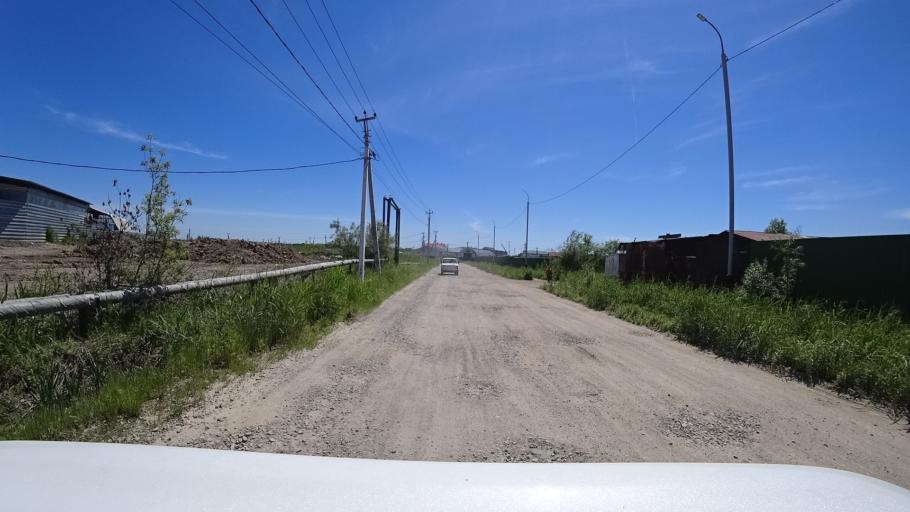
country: RU
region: Khabarovsk Krai
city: Topolevo
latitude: 48.5033
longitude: 135.1820
